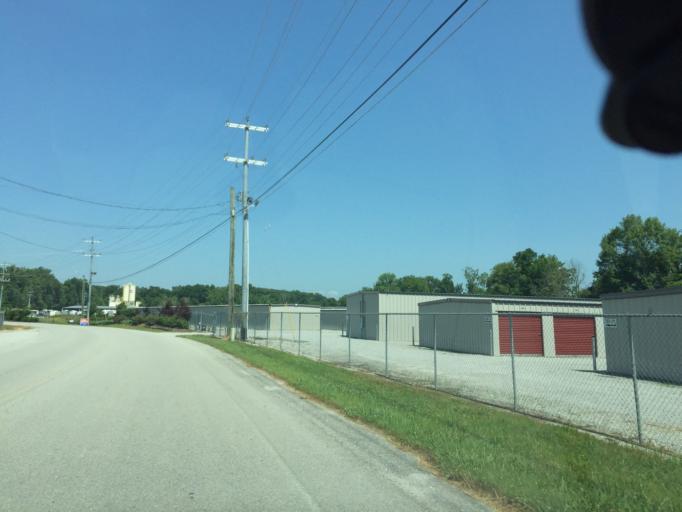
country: US
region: Tennessee
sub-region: Hamilton County
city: Collegedale
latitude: 35.0776
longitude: -85.0624
